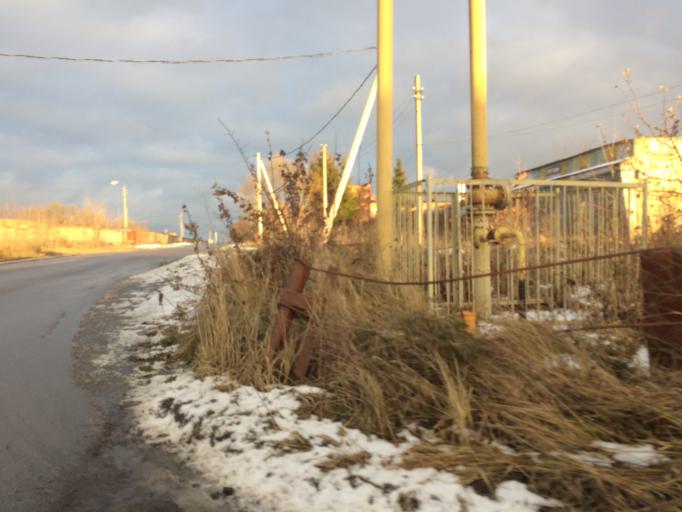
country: RU
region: Tula
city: Cherepet'
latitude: 54.1159
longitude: 36.3301
